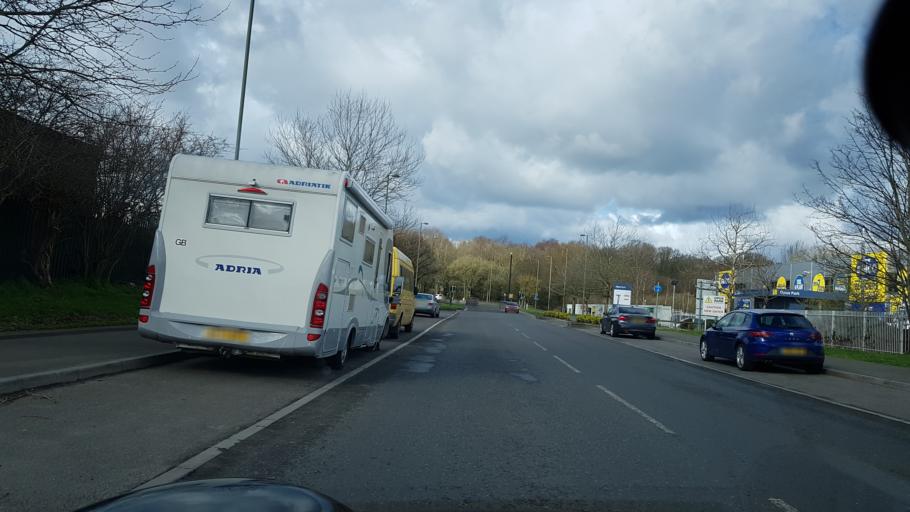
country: GB
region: England
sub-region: Surrey
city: Guildford
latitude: 51.2617
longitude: -0.5705
